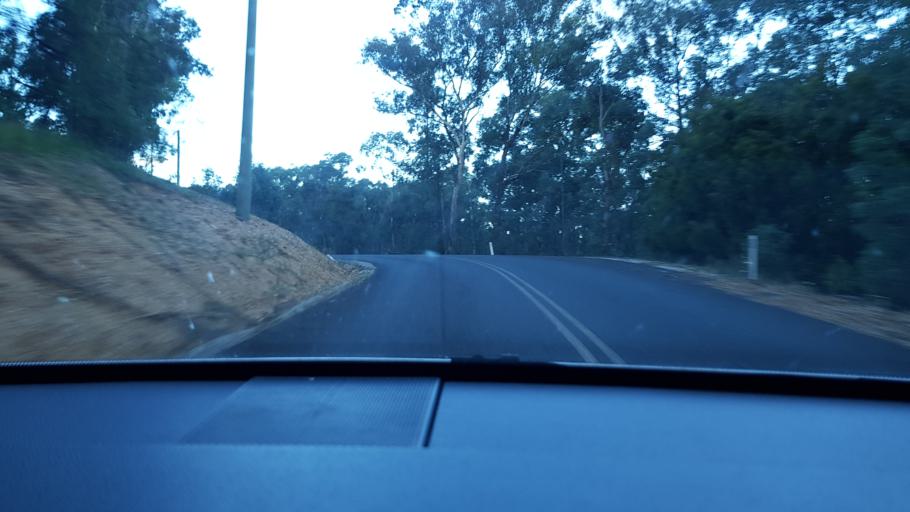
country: AU
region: New South Wales
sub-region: Lithgow
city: Portland
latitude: -33.2573
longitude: 150.1362
